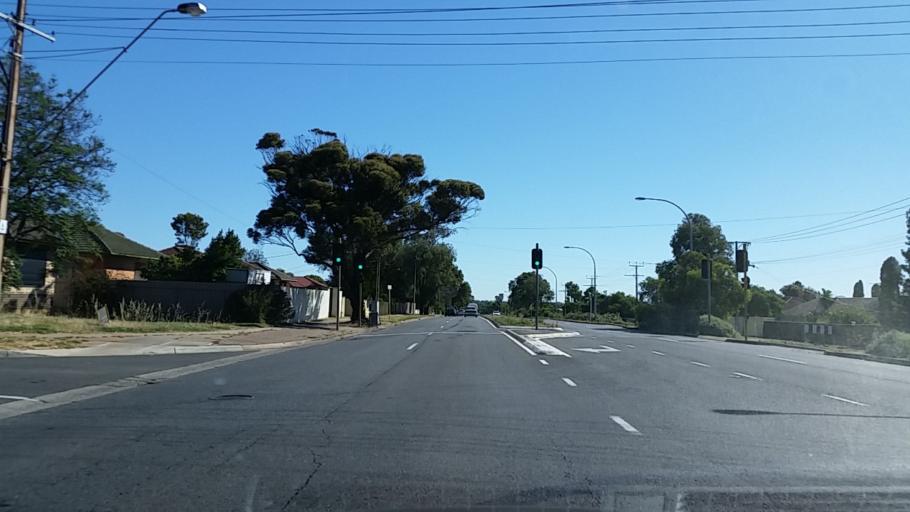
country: AU
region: South Australia
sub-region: Salisbury
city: Ingle Farm
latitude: -34.8005
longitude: 138.6549
